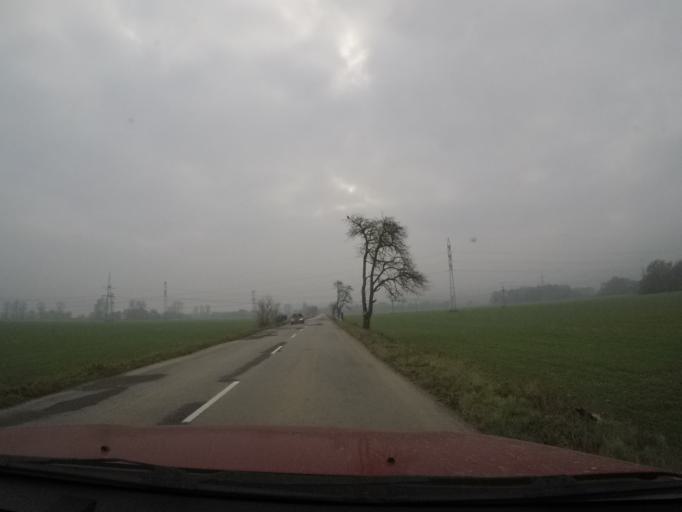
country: SK
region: Presovsky
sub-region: Okres Presov
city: Presov
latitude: 48.8665
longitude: 21.2711
